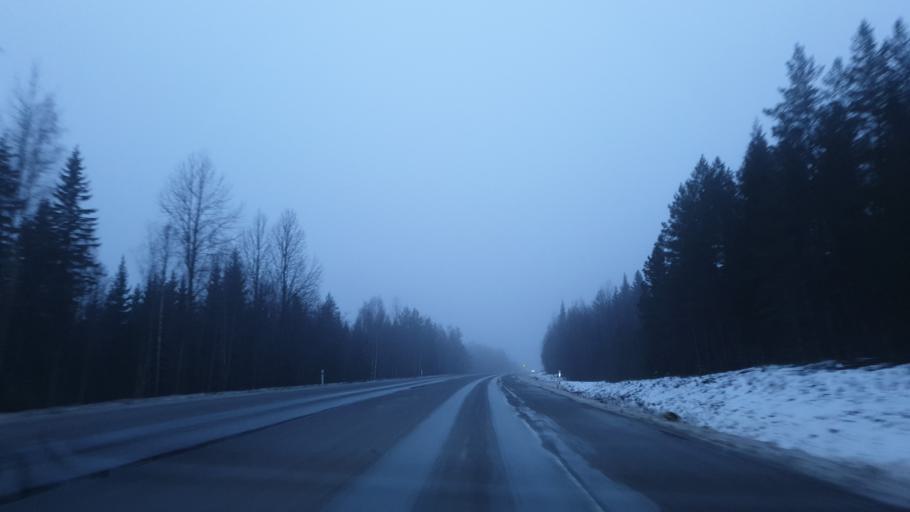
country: SE
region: Vaesterbotten
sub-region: Umea Kommun
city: Holmsund
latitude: 63.7629
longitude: 20.3424
